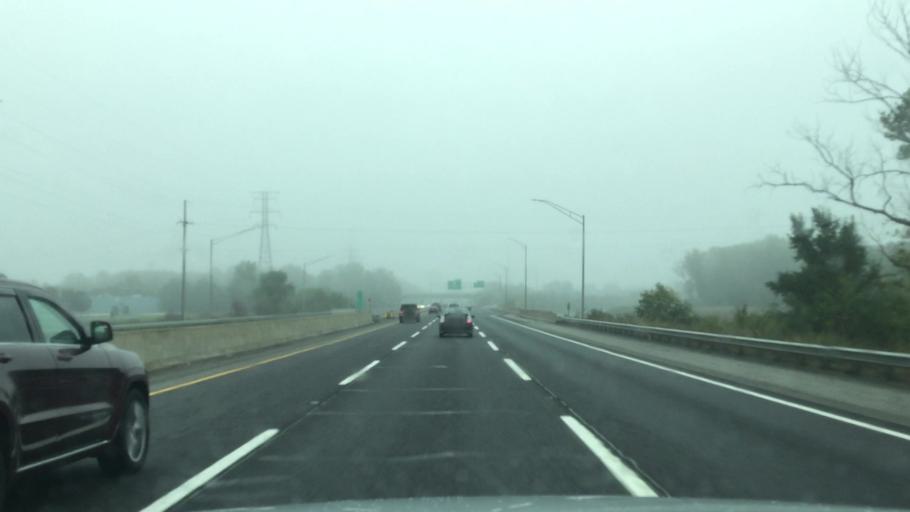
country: US
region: Indiana
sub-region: Lake County
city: Gary
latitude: 41.6102
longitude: -87.3669
